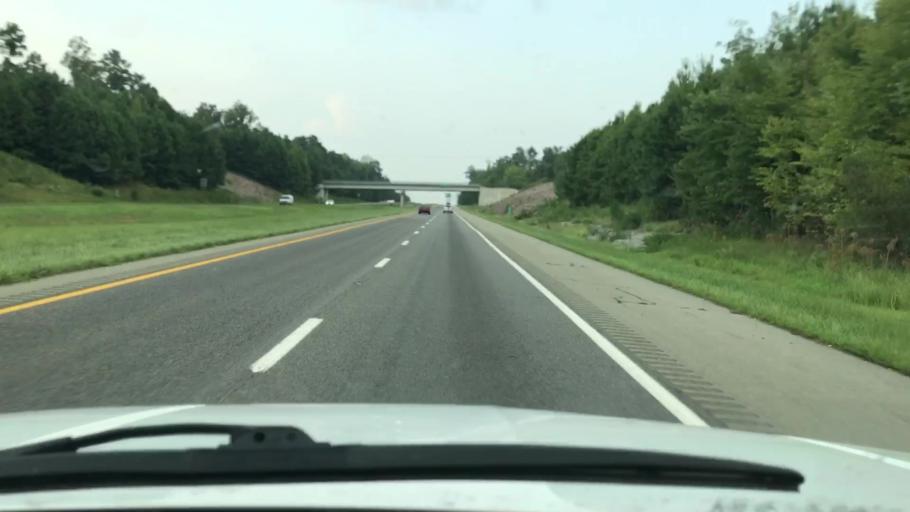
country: US
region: Virginia
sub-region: Henrico County
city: Short Pump
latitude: 37.5831
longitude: -77.6753
